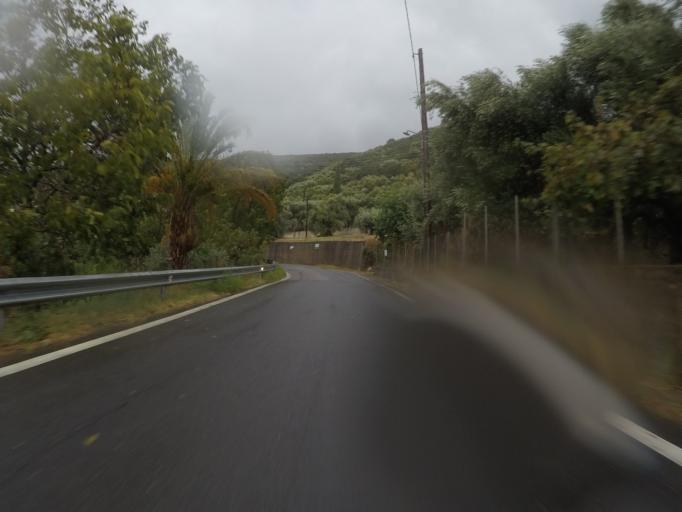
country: GR
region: Peloponnese
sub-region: Nomos Messinias
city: Kyparissia
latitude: 37.2514
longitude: 21.6866
